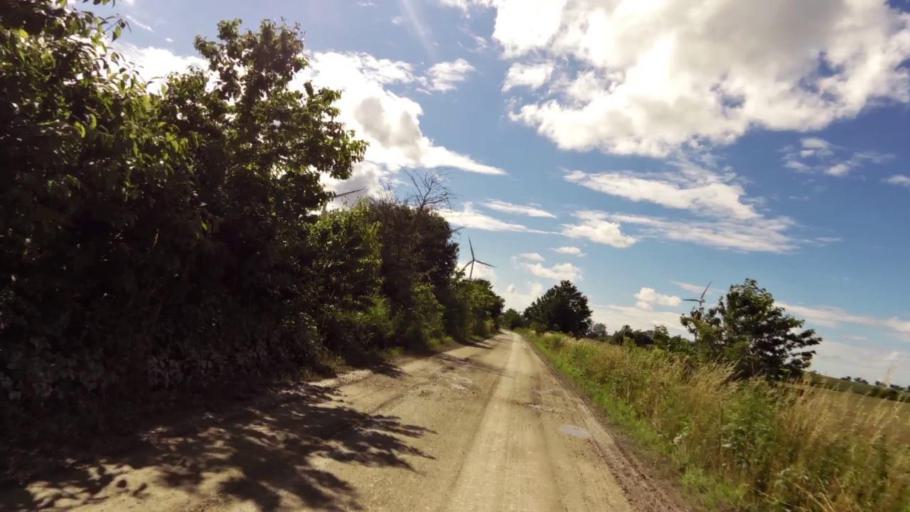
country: PL
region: Pomeranian Voivodeship
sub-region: Powiat slupski
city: Ustka
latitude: 54.5164
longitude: 16.7251
